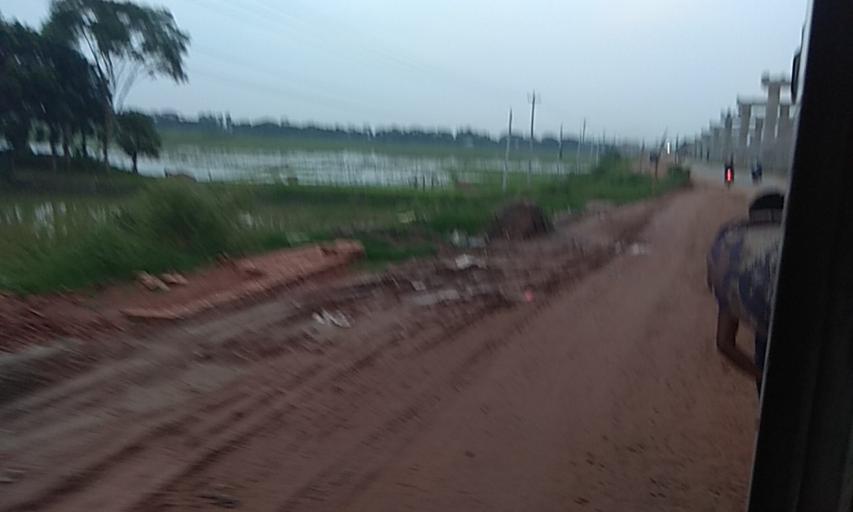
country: BD
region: Dhaka
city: Char Bhadrasan
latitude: 23.3843
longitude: 89.9975
